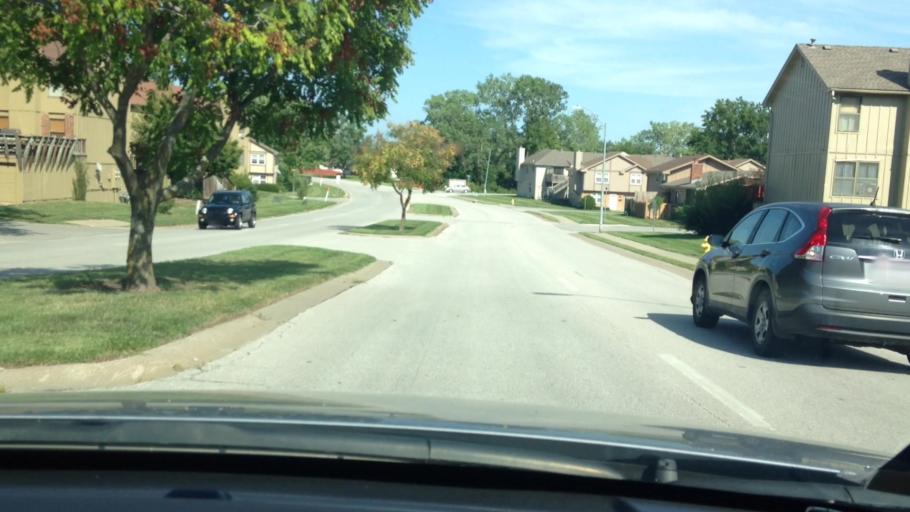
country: US
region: Missouri
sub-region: Jackson County
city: Grandview
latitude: 38.8705
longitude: -94.5237
